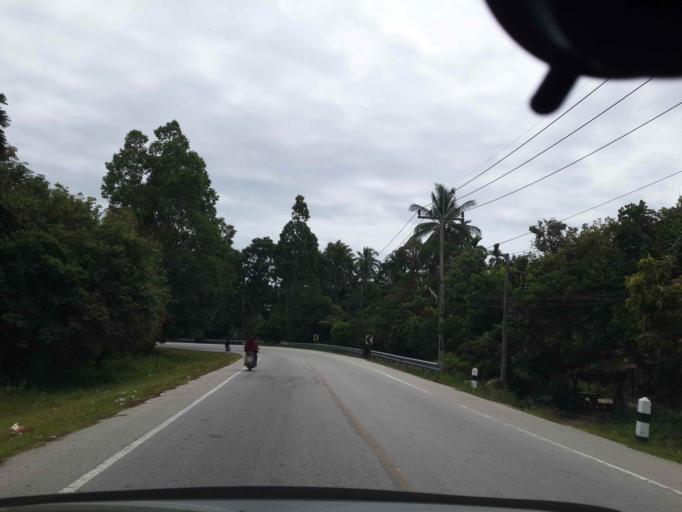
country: TH
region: Narathiwat
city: Rueso
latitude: 6.3567
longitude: 101.5804
